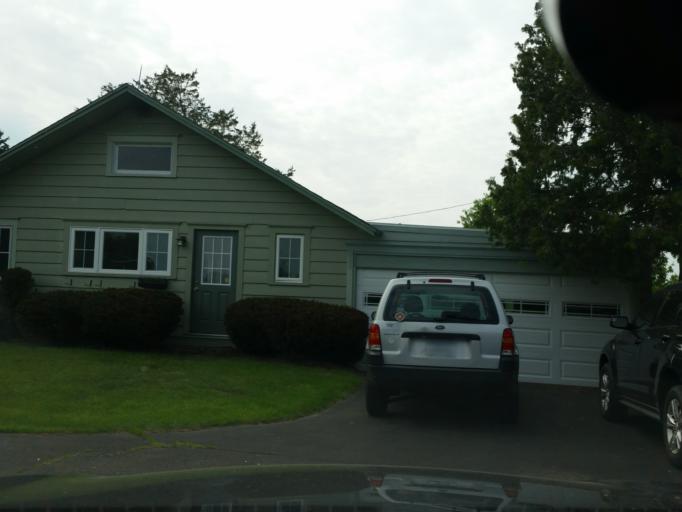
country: US
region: New York
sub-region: Chautauqua County
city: Mayville
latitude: 42.2348
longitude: -79.4406
